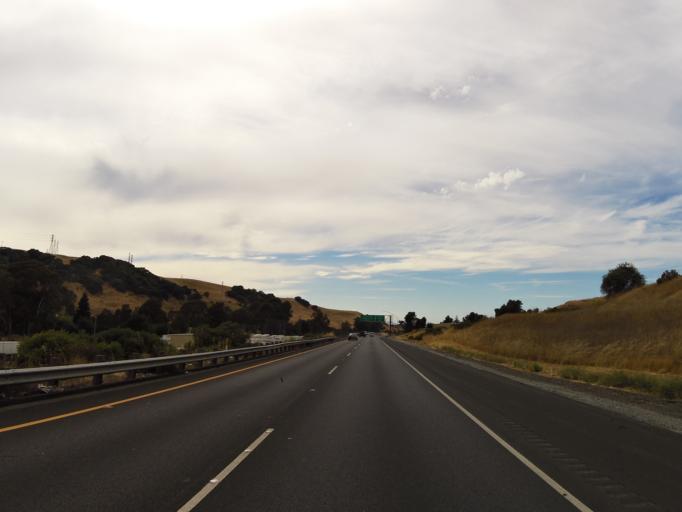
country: US
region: California
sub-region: Contra Costa County
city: Crockett
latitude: 38.0087
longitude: -122.2215
